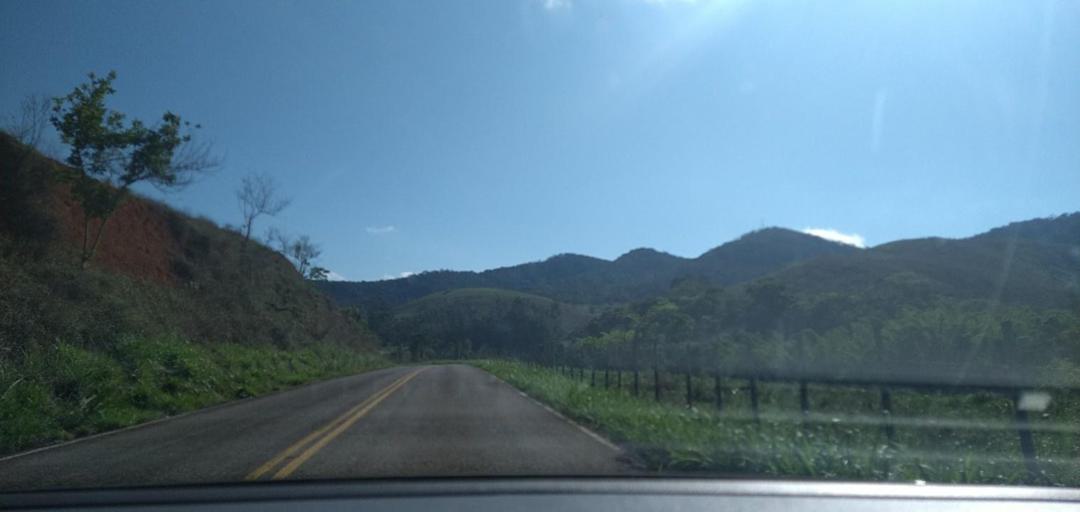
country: BR
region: Minas Gerais
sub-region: Alvinopolis
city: Alvinopolis
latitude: -20.1849
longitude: -42.9349
